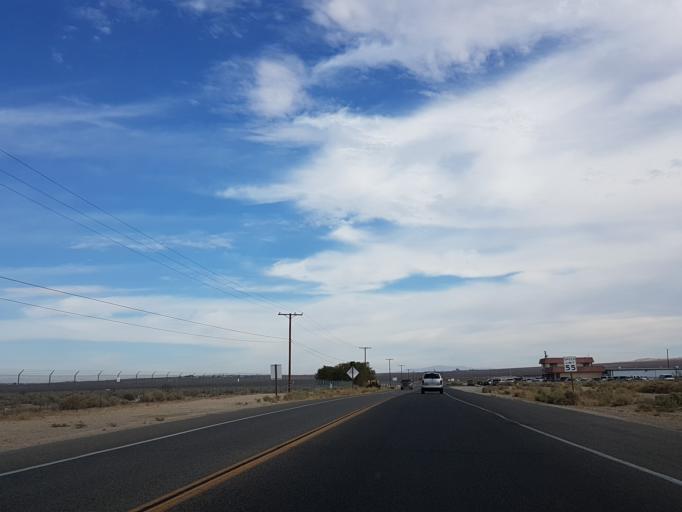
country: US
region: California
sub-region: Kern County
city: Ridgecrest
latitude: 35.6225
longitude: -117.6463
